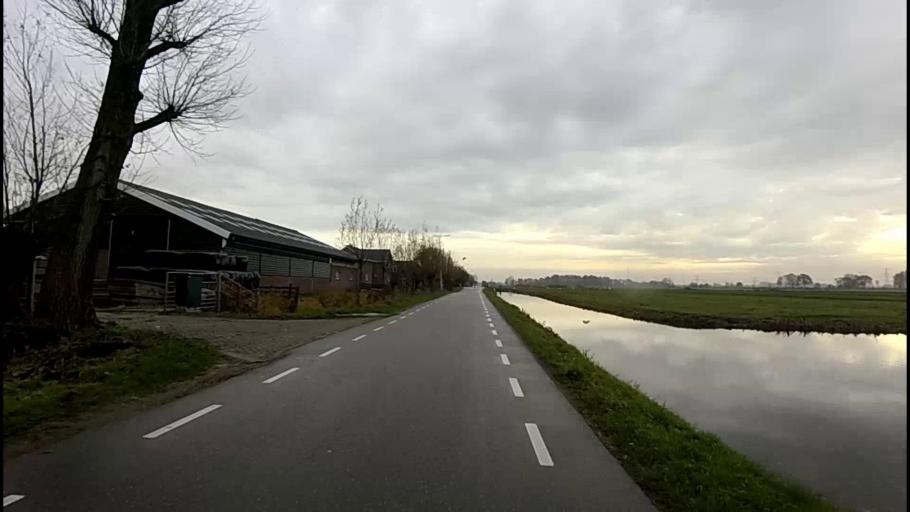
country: NL
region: South Holland
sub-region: Molenwaard
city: Nieuw-Lekkerland
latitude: 51.9227
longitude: 4.6520
